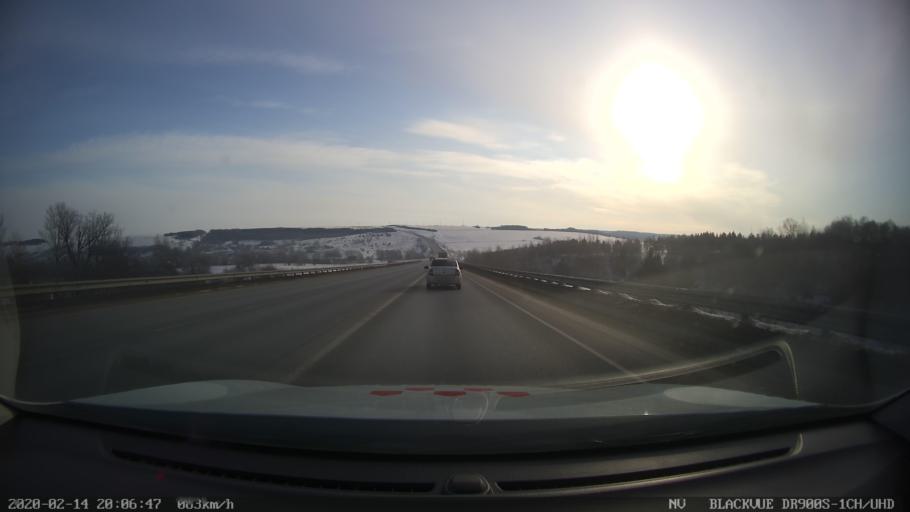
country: RU
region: Tatarstan
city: Verkhniy Uslon
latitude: 55.7216
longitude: 48.8329
